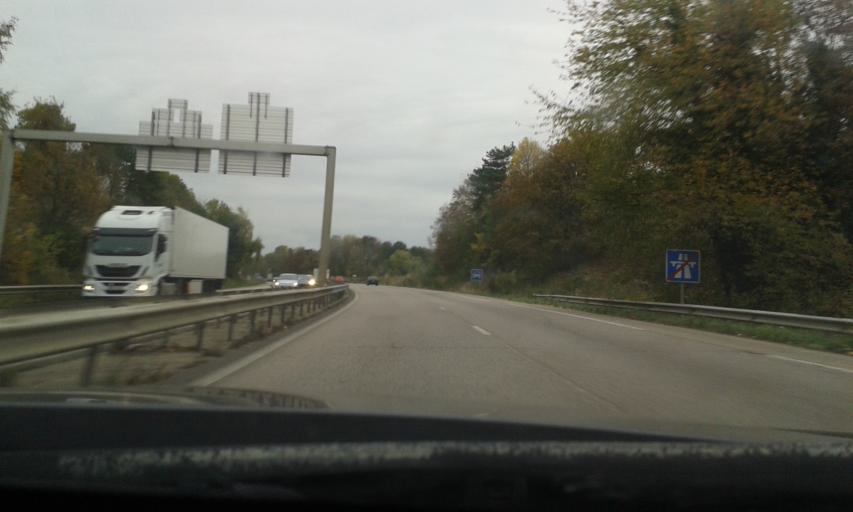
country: FR
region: Haute-Normandie
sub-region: Departement de la Seine-Maritime
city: Oissel
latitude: 49.3415
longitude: 1.0744
